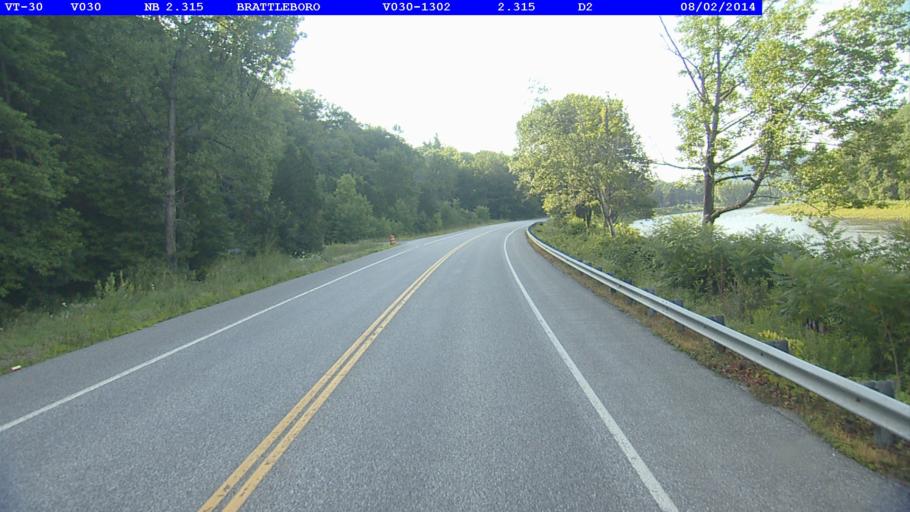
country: US
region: Vermont
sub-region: Windham County
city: West Brattleboro
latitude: 42.8827
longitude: -72.5865
